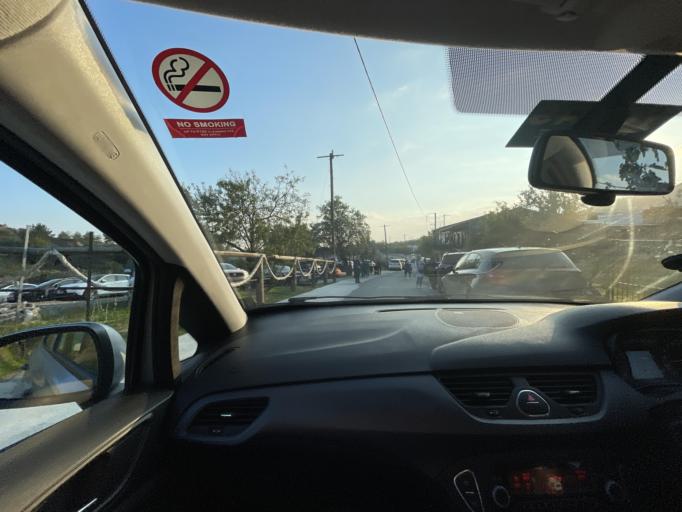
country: CY
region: Limassol
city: Pelendri
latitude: 34.8927
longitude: 32.9658
